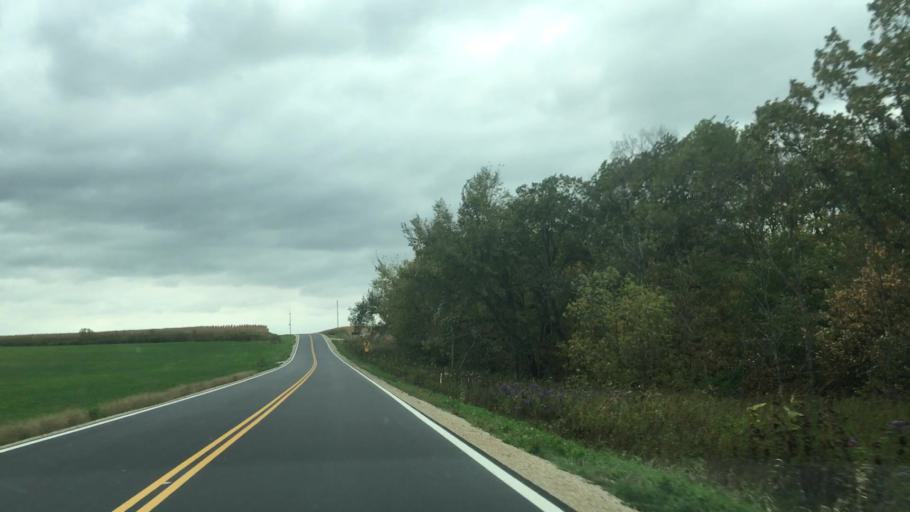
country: US
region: Minnesota
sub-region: Fillmore County
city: Preston
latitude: 43.7598
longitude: -92.0120
